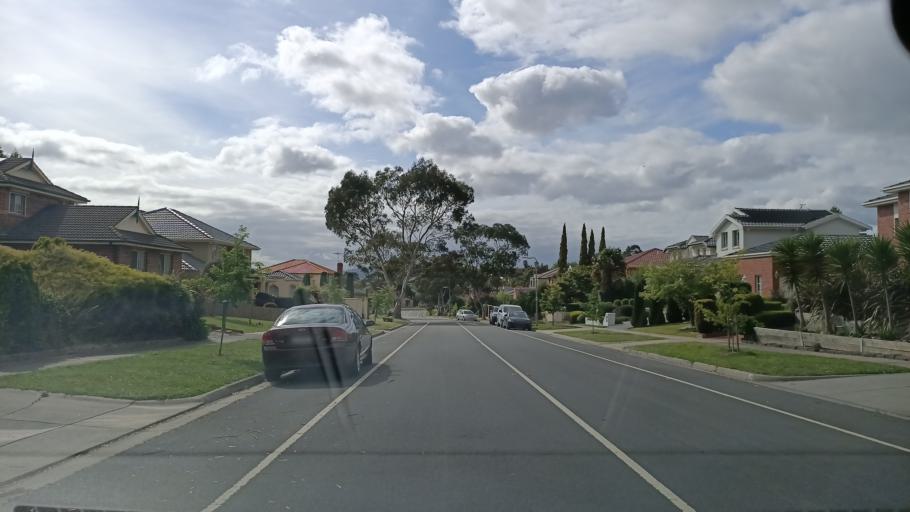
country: AU
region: Victoria
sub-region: Monash
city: Mulgrave
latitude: -37.9266
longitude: 145.1962
